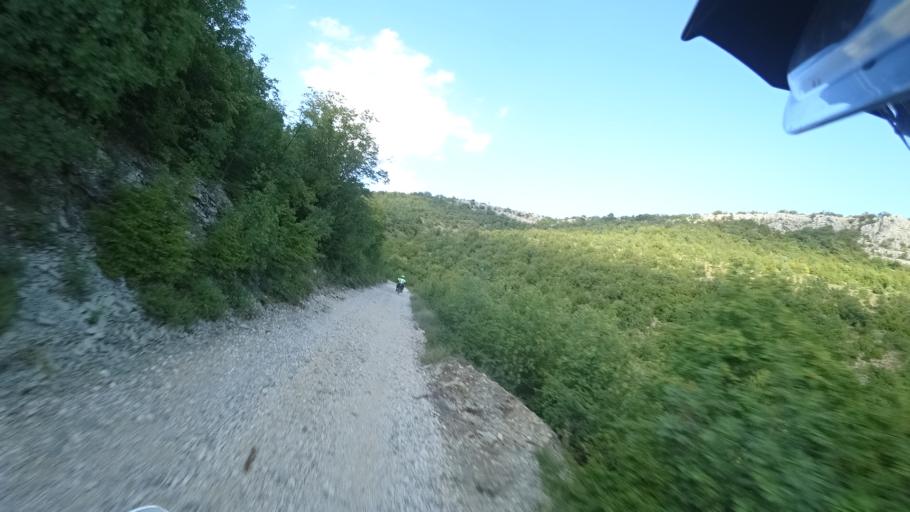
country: HR
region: Sibensko-Kniniska
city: Knin
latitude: 44.1769
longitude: 16.0729
